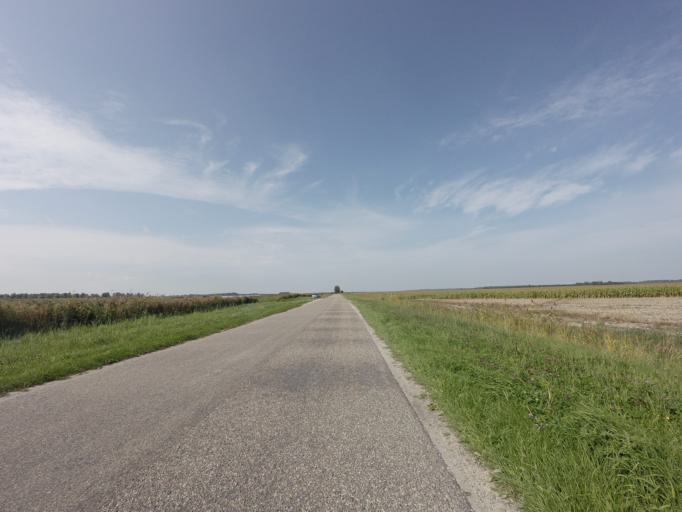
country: NL
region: Groningen
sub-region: Gemeente De Marne
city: Ulrum
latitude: 53.3451
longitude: 6.2768
